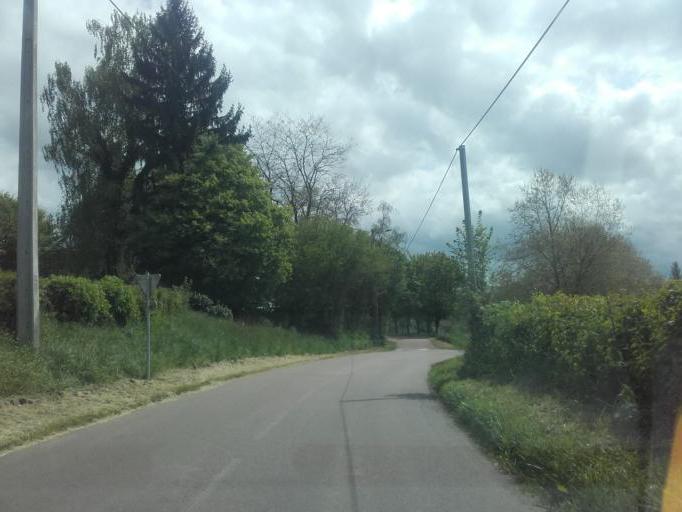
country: FR
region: Bourgogne
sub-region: Departement de Saone-et-Loire
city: Saint-Remy
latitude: 46.7628
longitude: 4.8149
